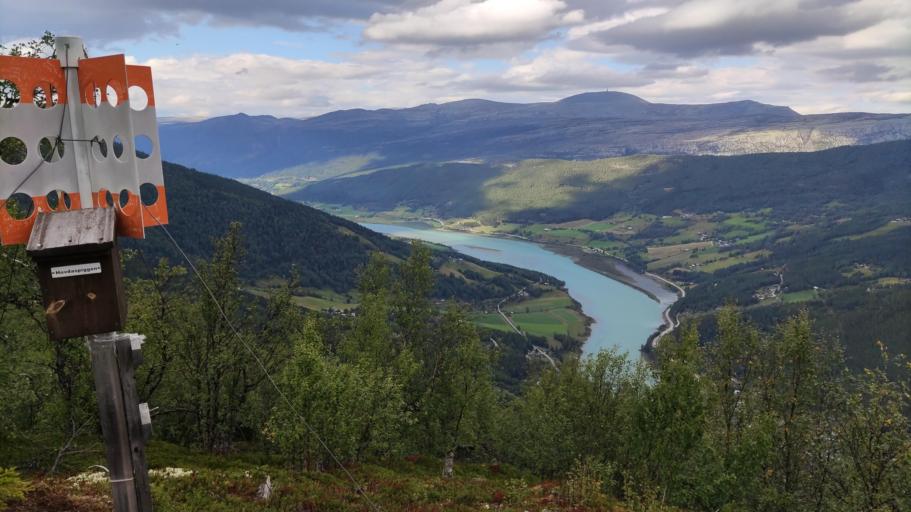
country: NO
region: Oppland
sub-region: Dovre
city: Dovre
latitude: 61.8047
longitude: 9.2686
